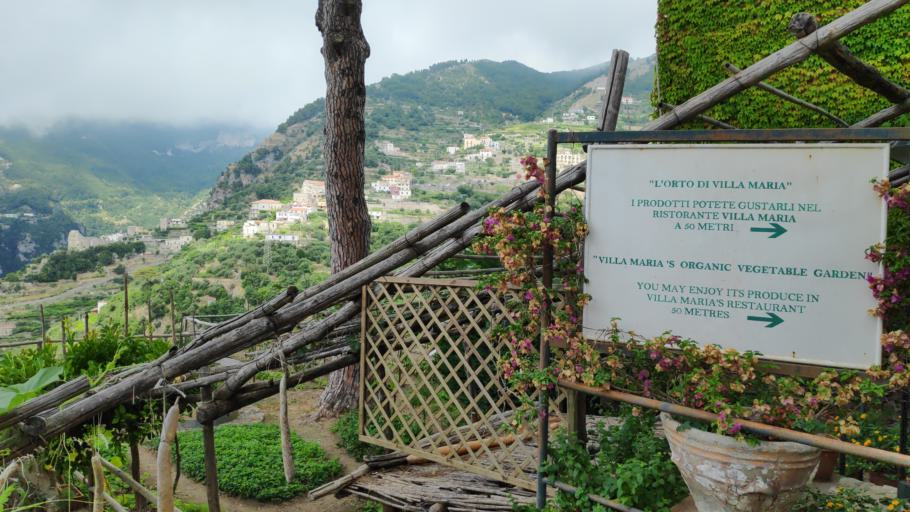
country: IT
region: Campania
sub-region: Provincia di Salerno
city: Ravello
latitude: 40.6461
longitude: 14.6106
